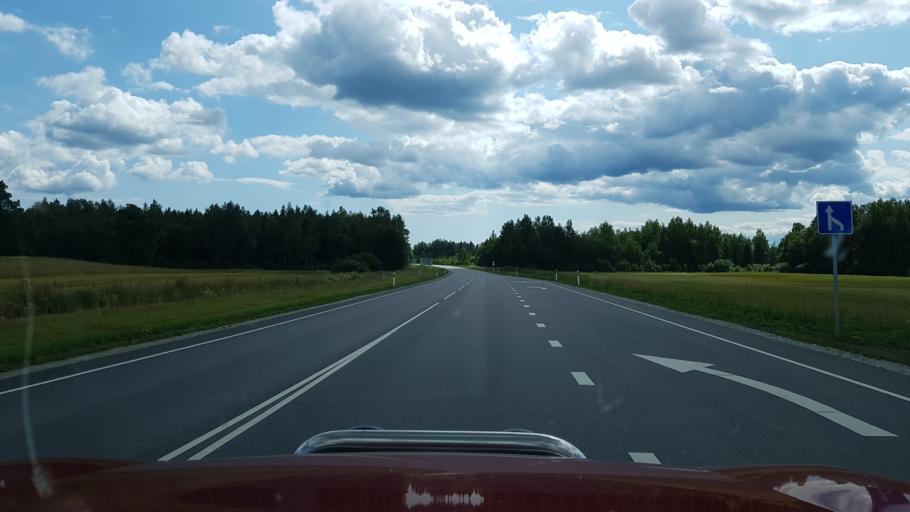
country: EE
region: Ida-Virumaa
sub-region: Johvi vald
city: Johvi
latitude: 59.2254
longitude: 27.3379
